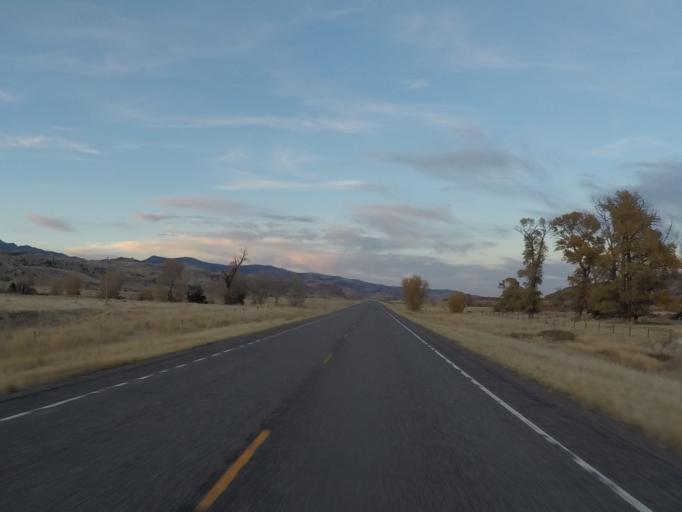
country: US
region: Montana
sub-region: Gallatin County
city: Bozeman
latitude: 45.2596
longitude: -110.8662
